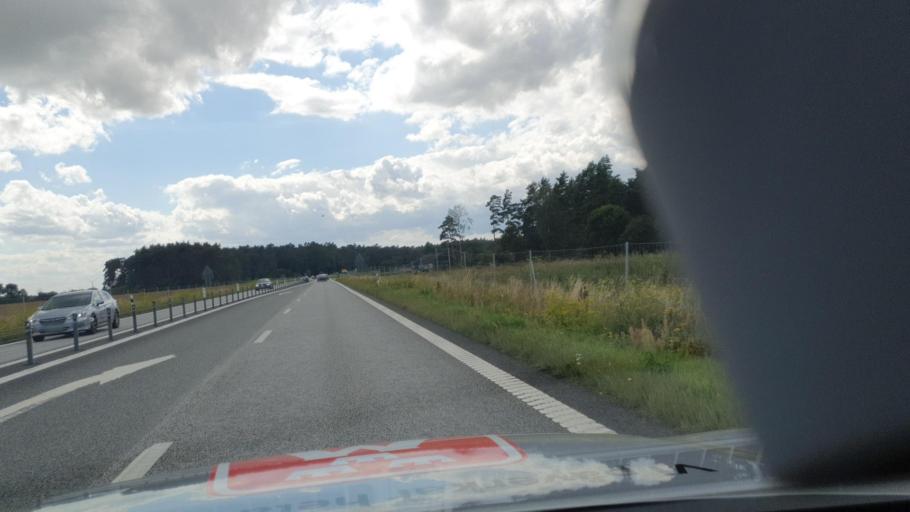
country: SE
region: Skane
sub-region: Bromolla Kommun
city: Bromoella
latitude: 56.0393
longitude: 14.3905
